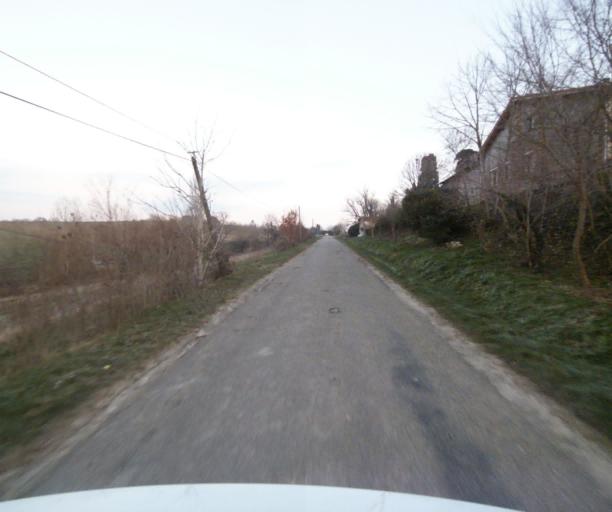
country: FR
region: Midi-Pyrenees
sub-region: Departement du Tarn-et-Garonne
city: Moissac
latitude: 44.1229
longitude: 1.0527
